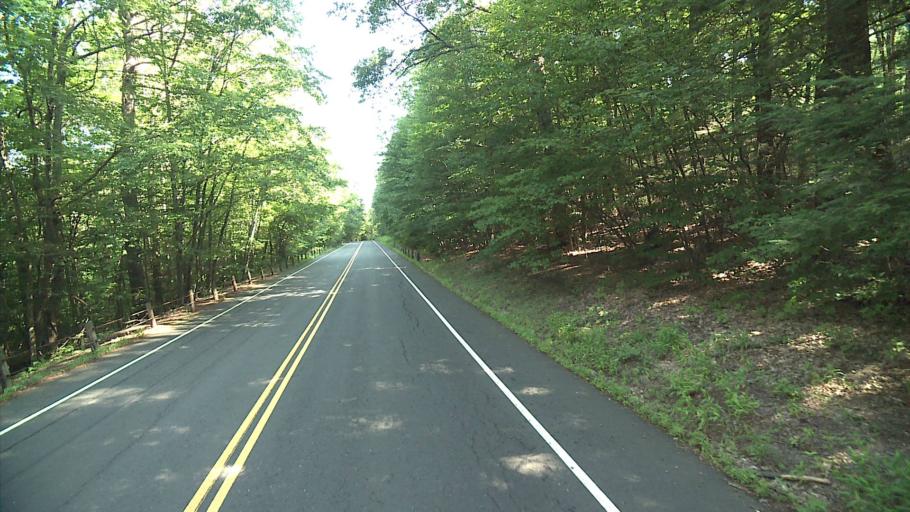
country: US
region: Massachusetts
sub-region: Hampden County
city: Granville
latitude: 42.0183
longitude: -72.9273
